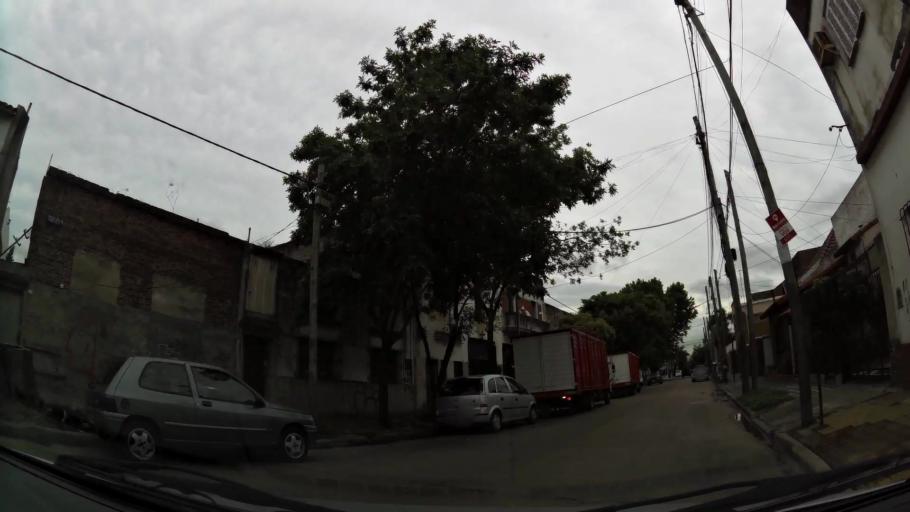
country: AR
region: Buenos Aires
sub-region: Partido de Lanus
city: Lanus
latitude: -34.6998
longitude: -58.3835
